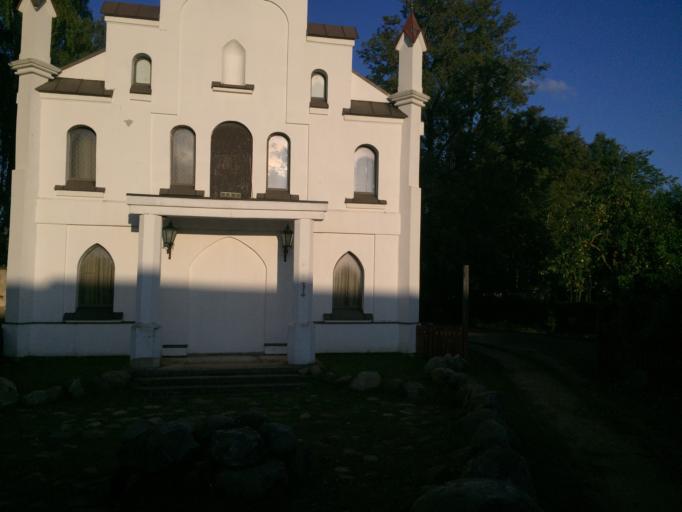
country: LV
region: Tukuma Rajons
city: Tukums
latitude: 56.8783
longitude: 23.2207
